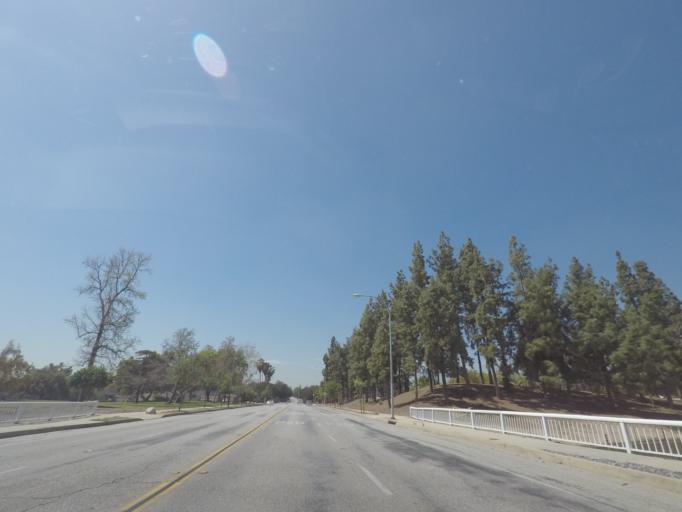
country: US
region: California
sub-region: Los Angeles County
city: East Pasadena
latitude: 34.1585
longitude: -118.0875
